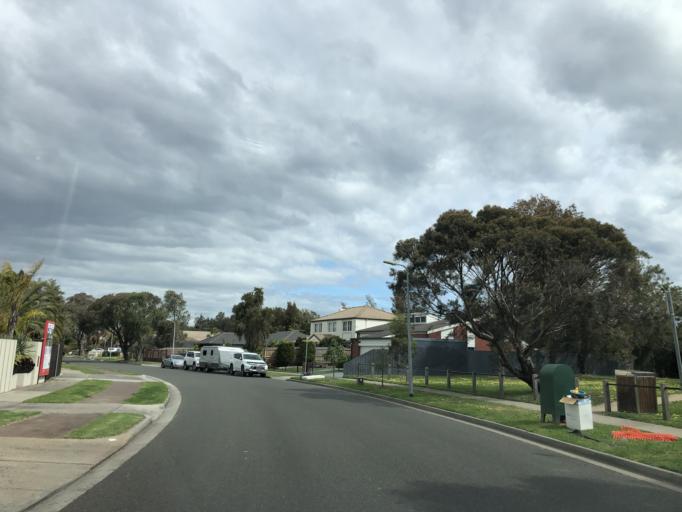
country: AU
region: Victoria
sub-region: Kingston
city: Carrum
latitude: -38.0784
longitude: 145.1346
